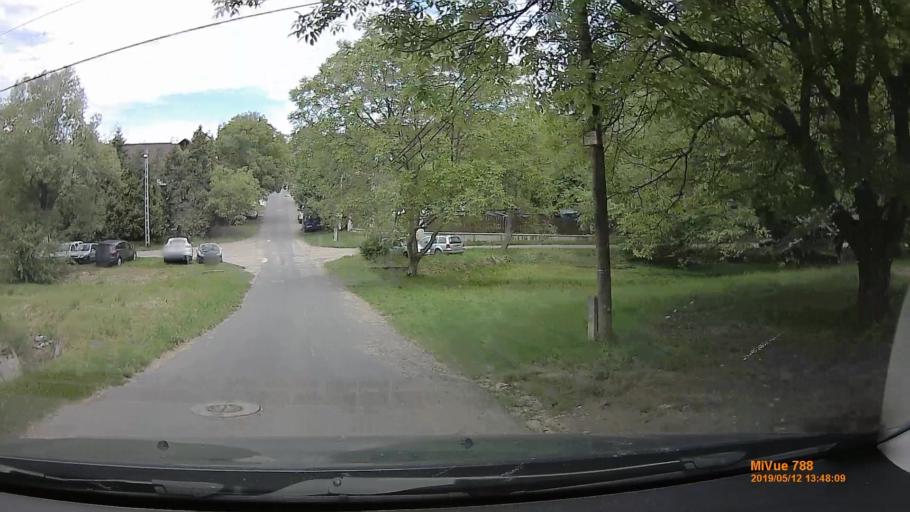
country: HU
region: Pest
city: Pecel
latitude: 47.4864
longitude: 19.3004
